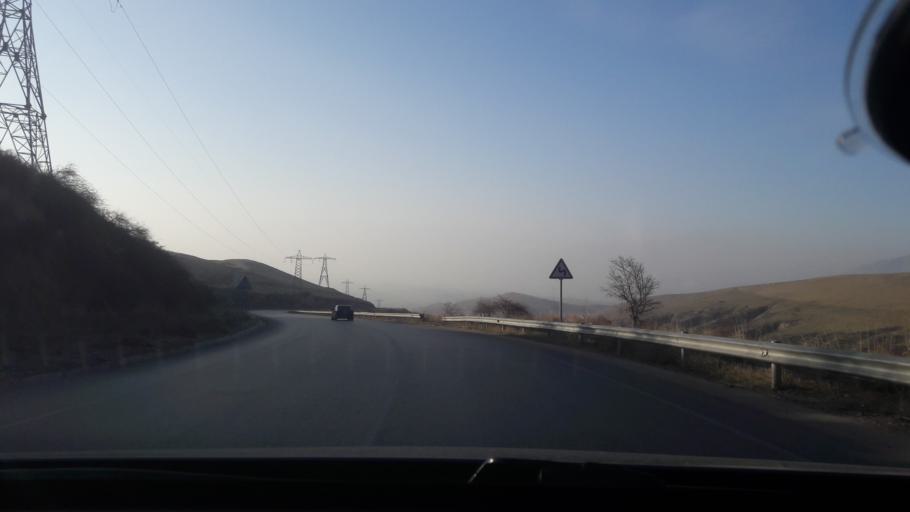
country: TJ
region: Khatlon
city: Danghara
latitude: 38.1963
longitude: 69.2916
